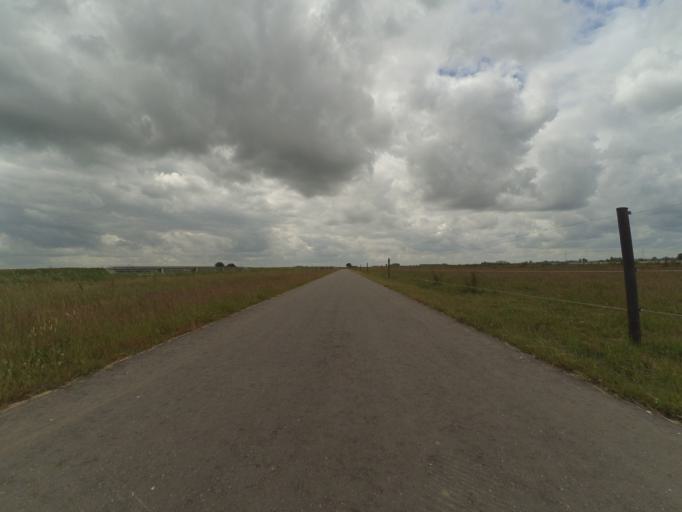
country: NL
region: South Holland
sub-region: Gemeente Hardinxveld-Giessendam
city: Boven-Hardinxveld
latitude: 51.8013
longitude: 4.8645
